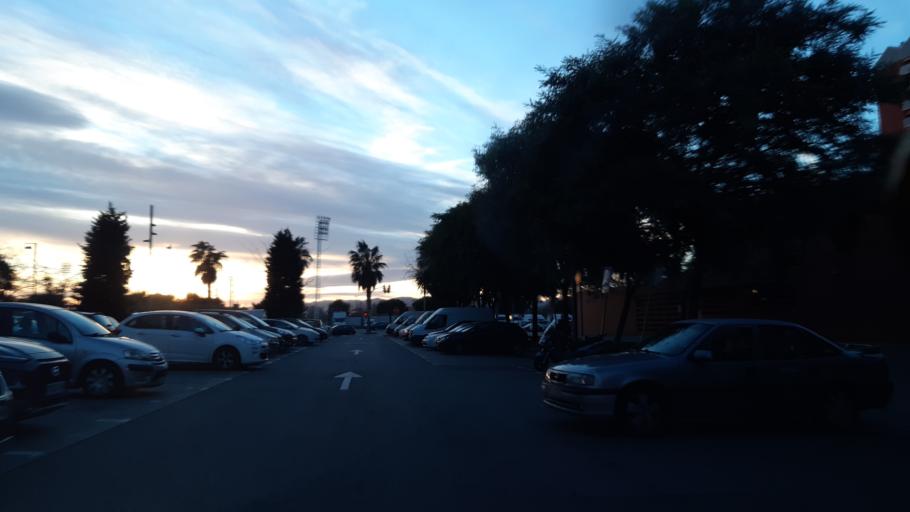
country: ES
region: Catalonia
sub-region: Provincia de Barcelona
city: L'Hospitalet de Llobregat
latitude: 41.3496
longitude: 2.1070
